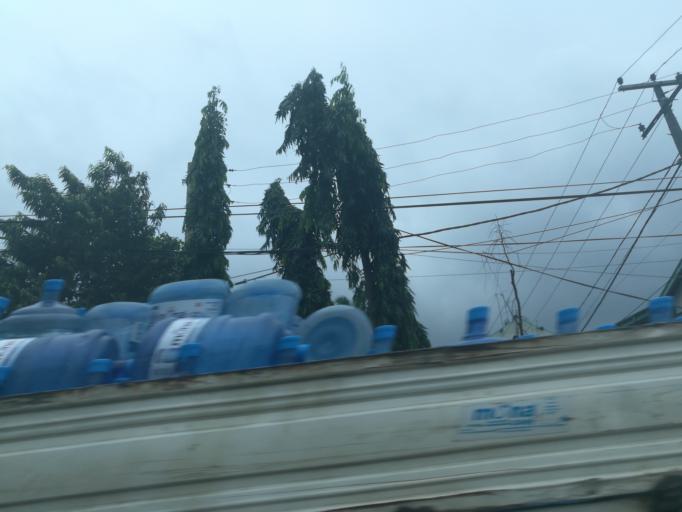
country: NG
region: Lagos
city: Ikeja
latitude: 6.6113
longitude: 3.3451
